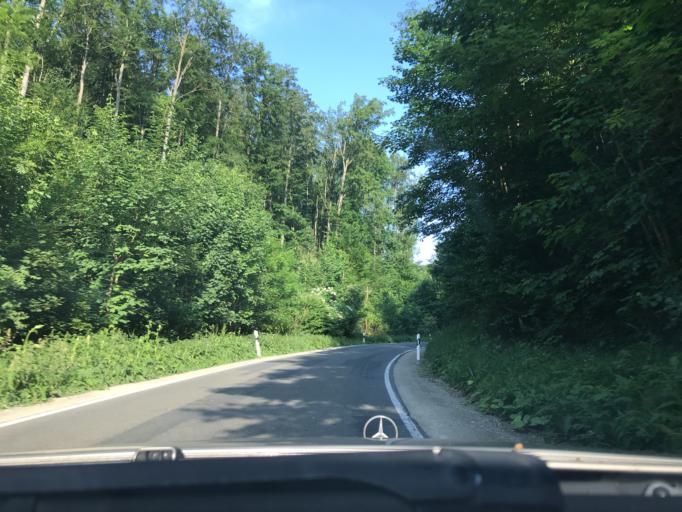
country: DE
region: Thuringia
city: Kleinbartloff
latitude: 51.3384
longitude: 10.3761
